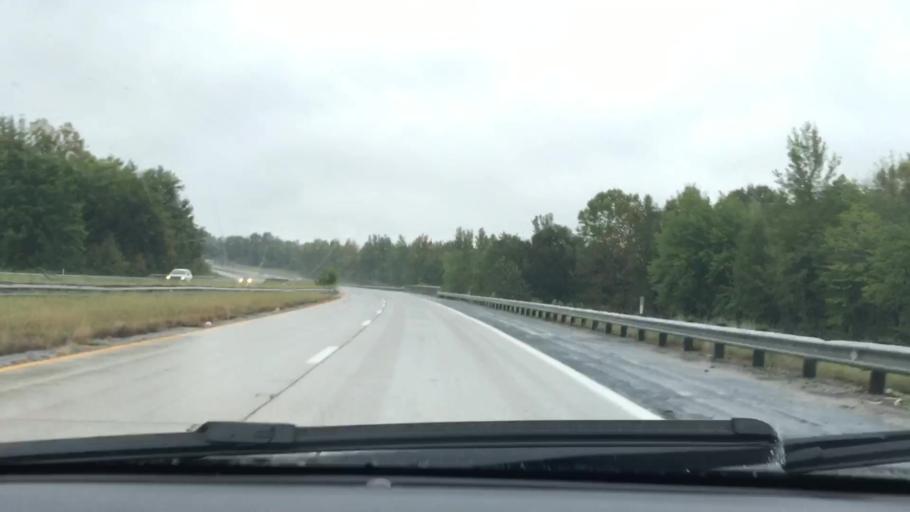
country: US
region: Kentucky
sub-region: Hopkins County
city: Nortonville
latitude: 37.1480
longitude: -87.4653
